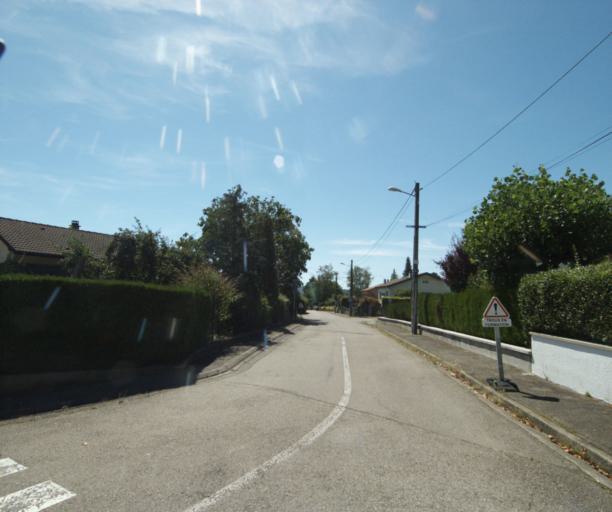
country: FR
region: Lorraine
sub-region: Departement des Vosges
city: Epinal
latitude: 48.1960
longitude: 6.4550
